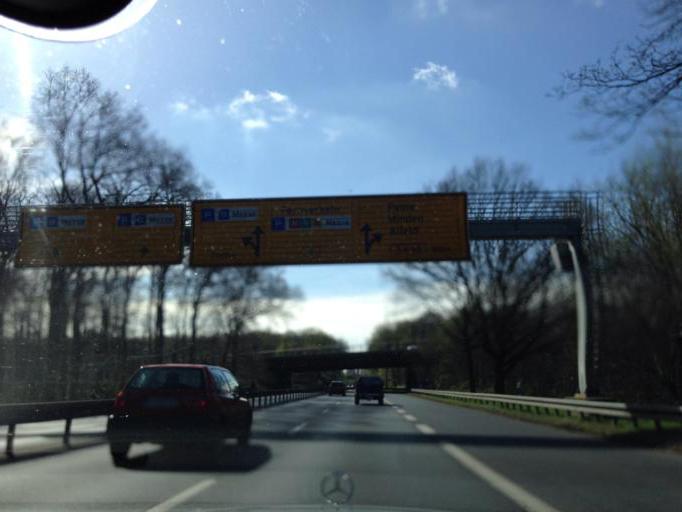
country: DE
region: Lower Saxony
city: Laatzen
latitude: 52.3617
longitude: 9.7826
